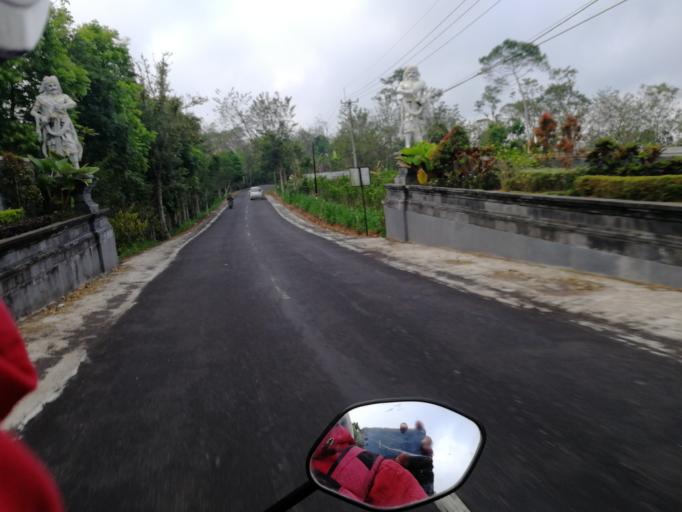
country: ID
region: Bali
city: Banjar Taro Kelod
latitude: -8.2535
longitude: 115.2452
